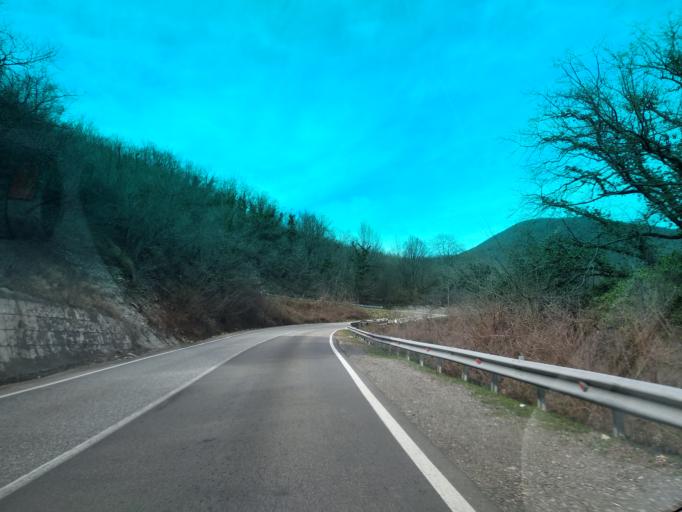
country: RU
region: Krasnodarskiy
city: Shepsi
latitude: 44.0721
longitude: 39.1402
